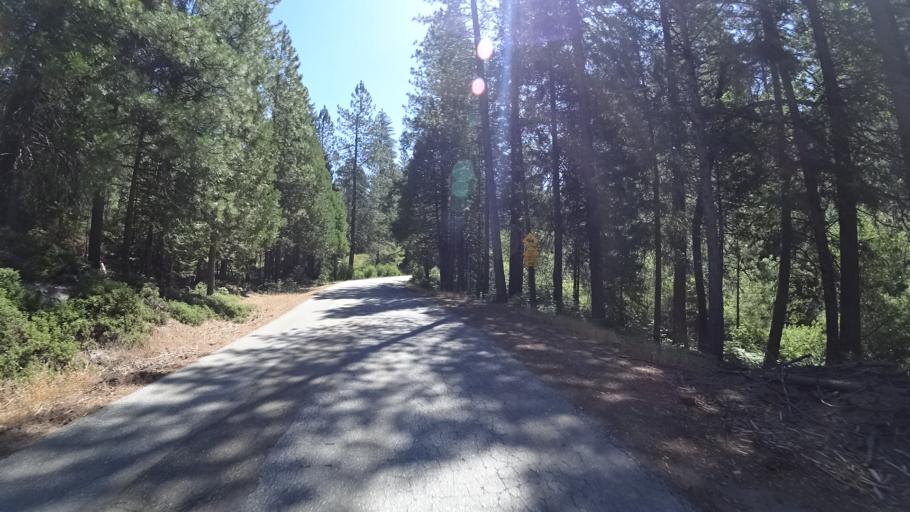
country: US
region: California
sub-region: Amador County
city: Pioneer
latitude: 38.4330
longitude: -120.4626
